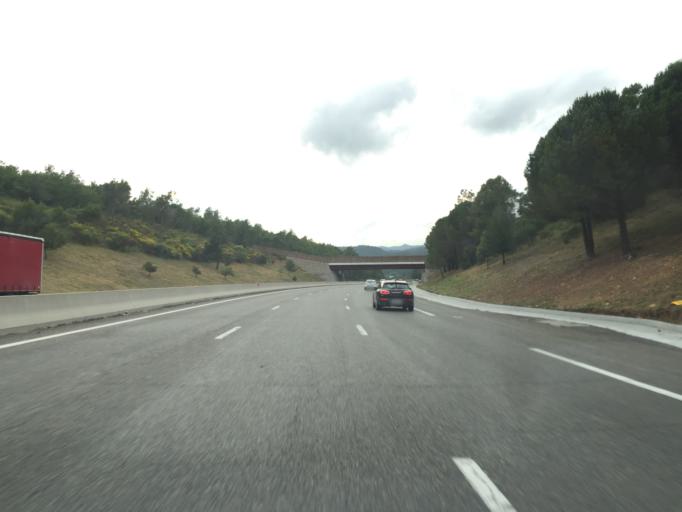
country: FR
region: Provence-Alpes-Cote d'Azur
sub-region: Departement du Var
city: Camps-la-Source
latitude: 43.4132
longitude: 6.1361
